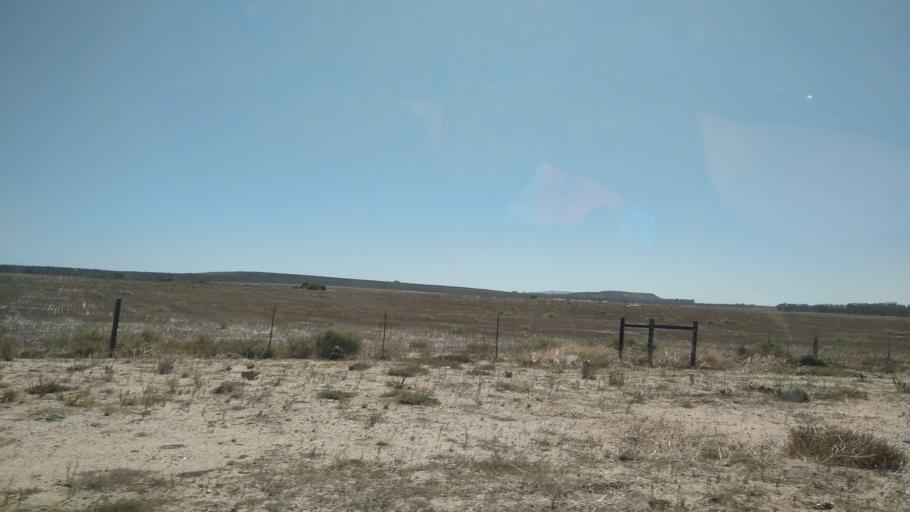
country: ZA
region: Western Cape
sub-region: West Coast District Municipality
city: Vredenburg
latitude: -32.9901
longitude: 18.1353
